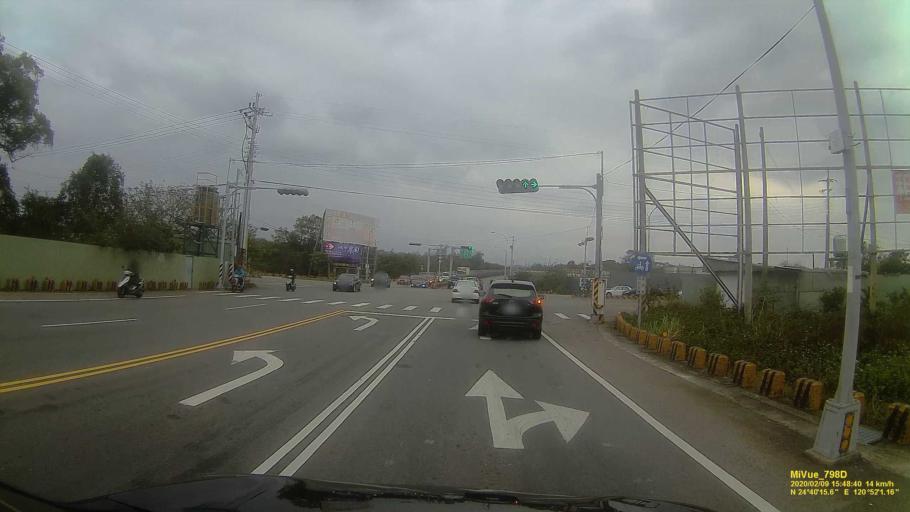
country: TW
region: Taiwan
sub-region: Miaoli
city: Miaoli
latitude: 24.6709
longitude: 120.8670
